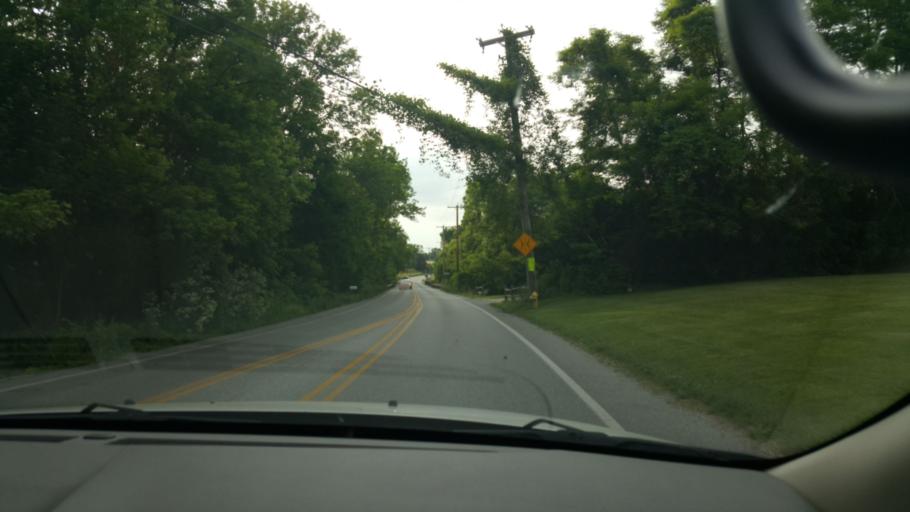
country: US
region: Pennsylvania
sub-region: York County
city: Shiloh
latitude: 39.9997
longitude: -76.7976
